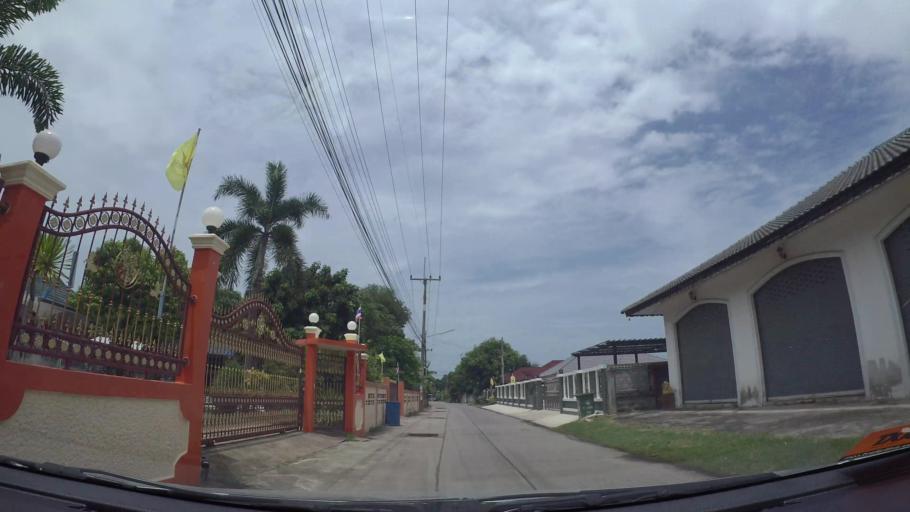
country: TH
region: Chon Buri
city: Sattahip
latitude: 12.6845
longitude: 100.9024
